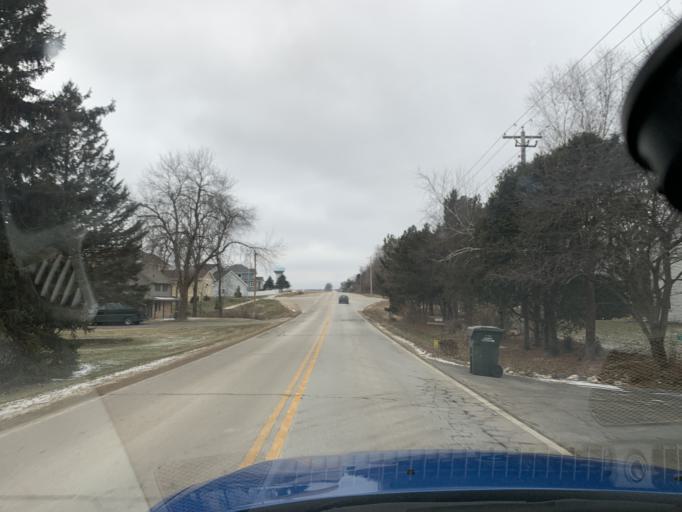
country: US
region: Wisconsin
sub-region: Dane County
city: Middleton
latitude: 43.0748
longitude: -89.5554
